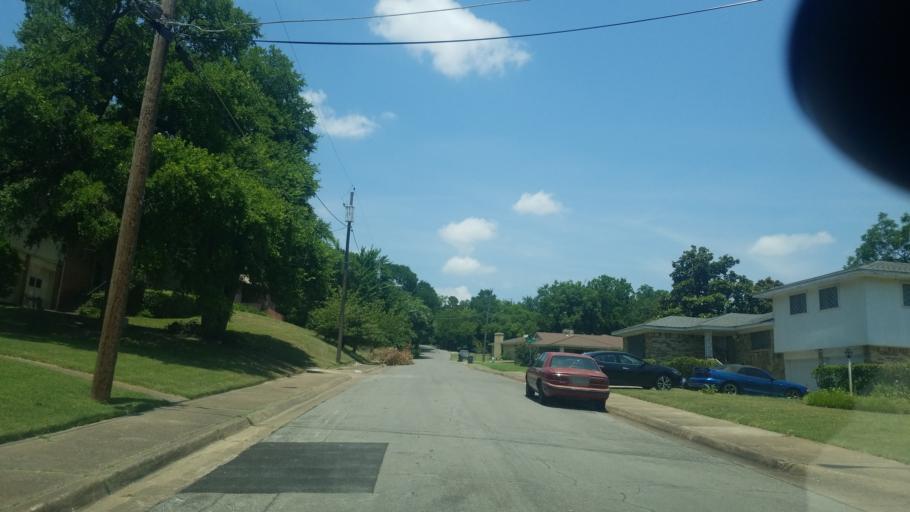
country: US
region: Texas
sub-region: Dallas County
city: Dallas
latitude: 32.7313
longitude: -96.7918
